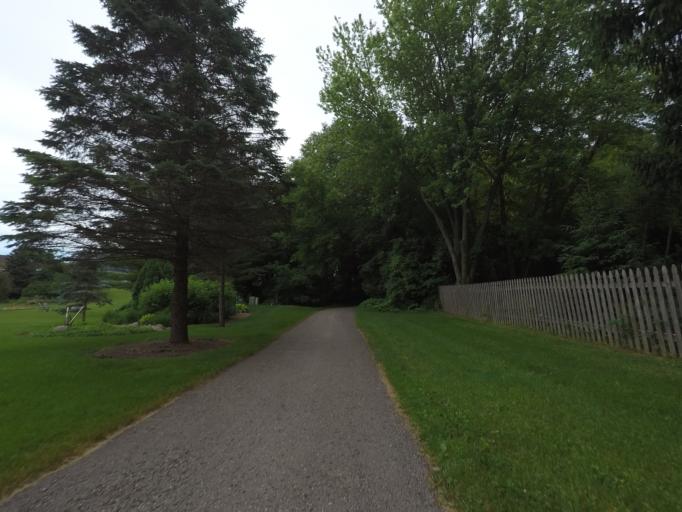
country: US
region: Wisconsin
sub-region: Dane County
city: Middleton
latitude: 43.0837
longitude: -89.5080
